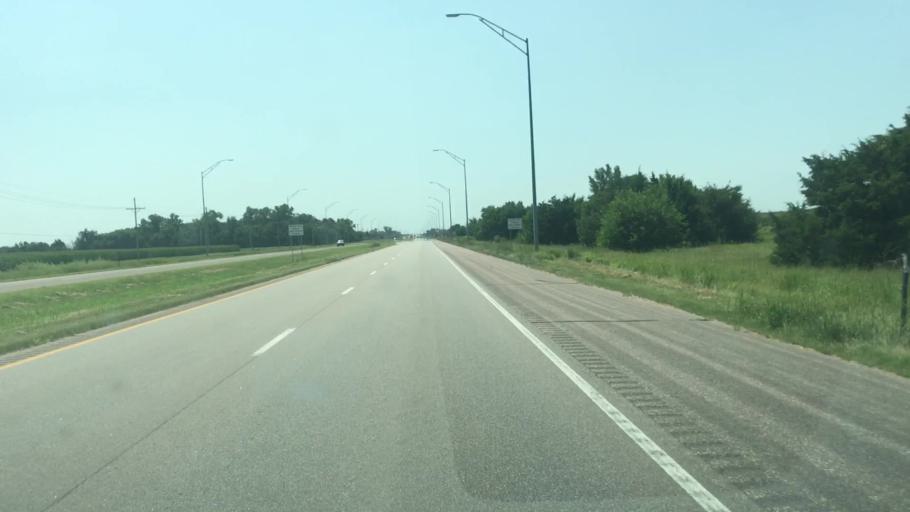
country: US
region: Nebraska
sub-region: Hall County
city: Grand Island
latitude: 40.8479
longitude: -98.3787
